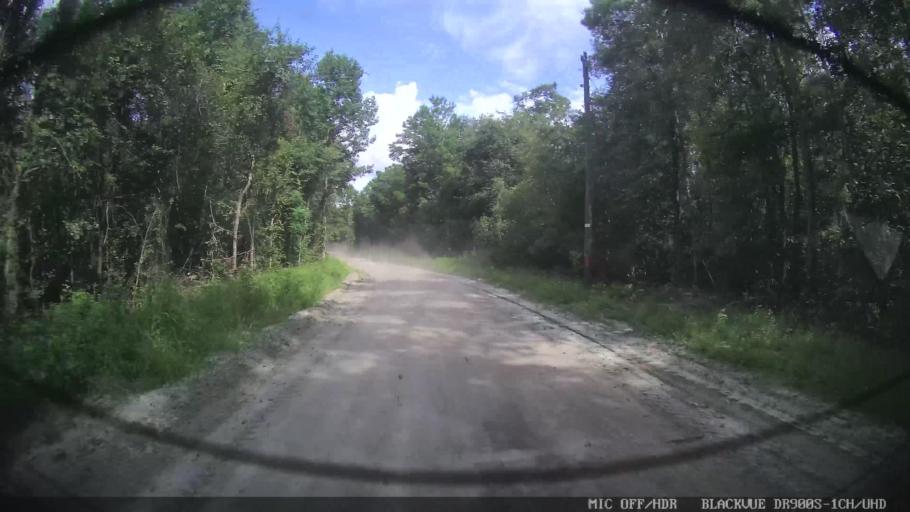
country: US
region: Florida
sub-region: Hamilton County
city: Jasper
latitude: 30.5512
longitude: -83.0883
